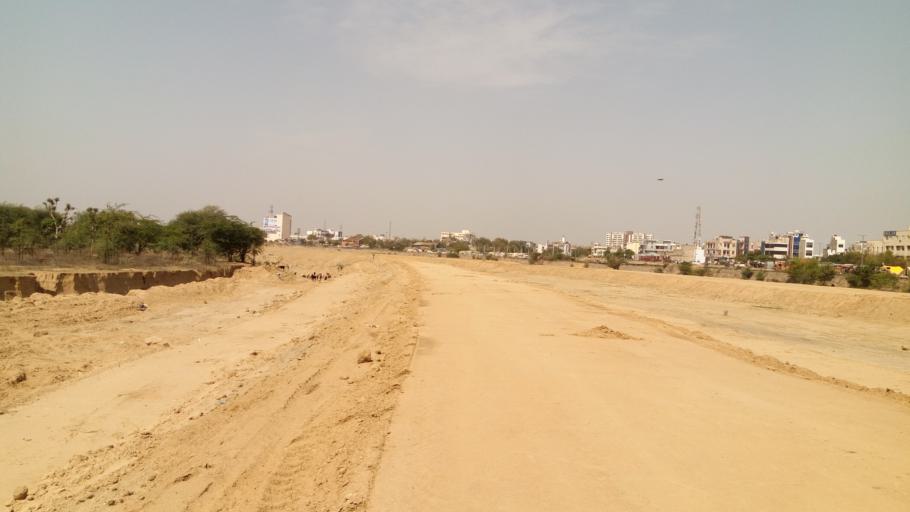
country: IN
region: Rajasthan
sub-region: Jaipur
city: Jaipur
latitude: 26.7944
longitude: 75.8204
